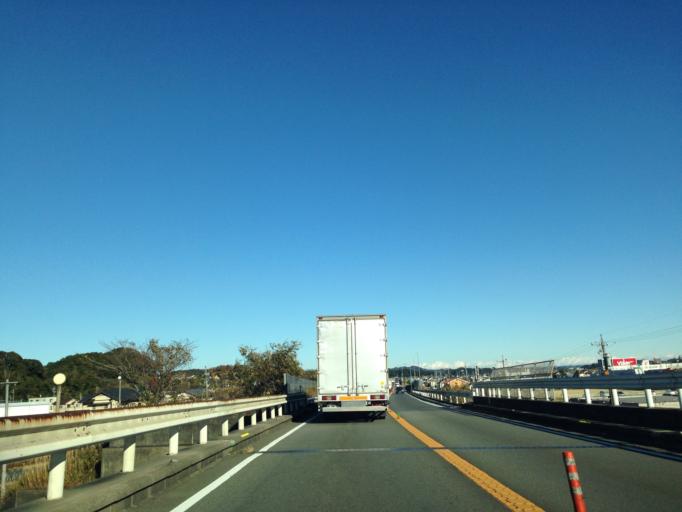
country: JP
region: Shizuoka
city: Kakegawa
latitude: 34.7767
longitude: 137.9844
